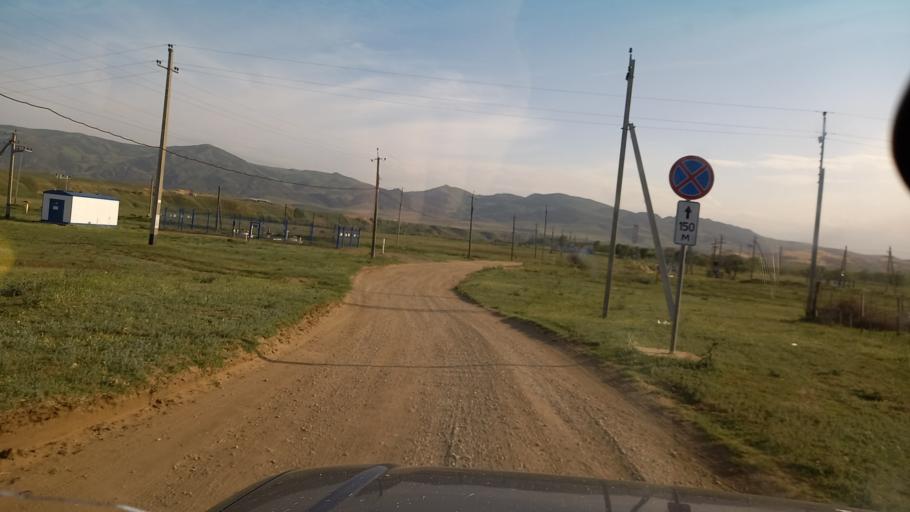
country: RU
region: Dagestan
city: Korkmaskala
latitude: 43.0250
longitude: 47.2644
